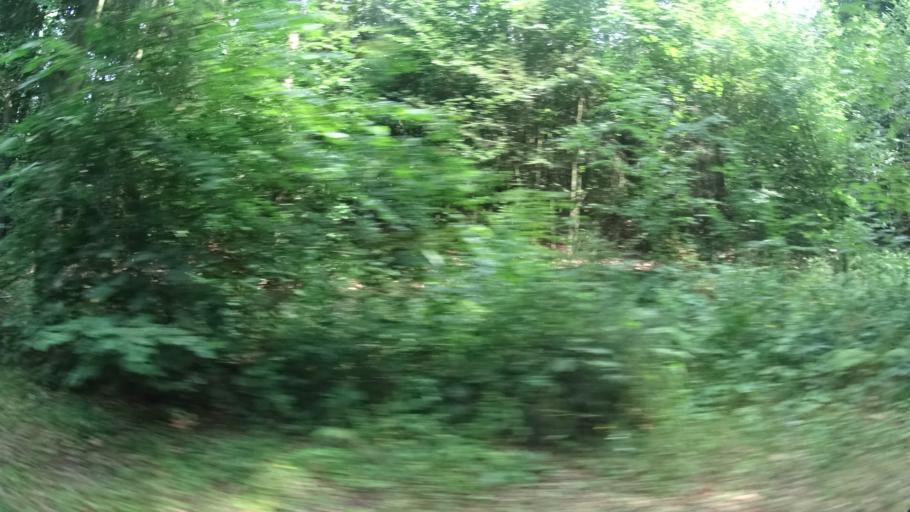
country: DE
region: Hesse
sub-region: Regierungsbezirk Giessen
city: Lauterbach
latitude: 50.6073
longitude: 9.4324
